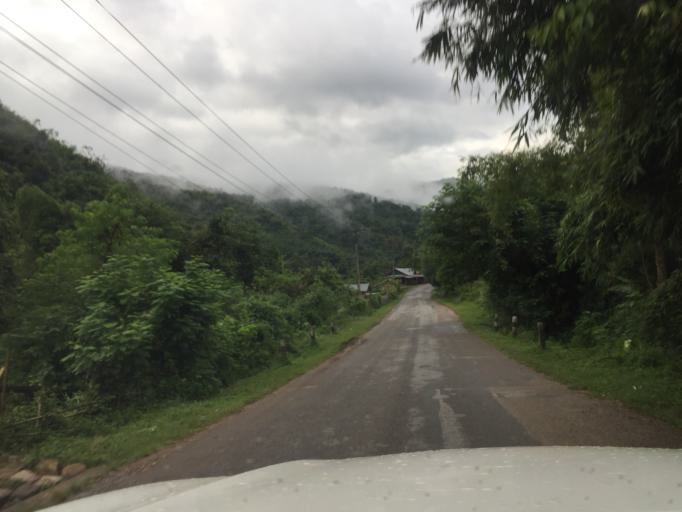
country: LA
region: Oudomxai
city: Muang La
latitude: 20.8736
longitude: 102.1344
